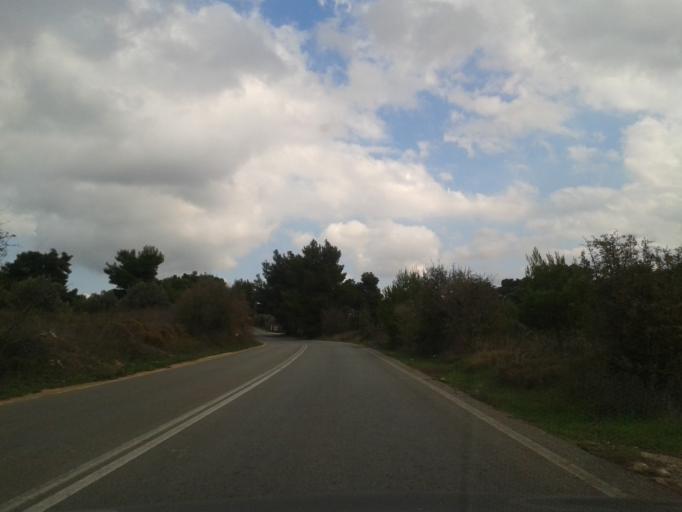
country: GR
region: Attica
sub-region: Nomarchia Anatolikis Attikis
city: Kapandriti
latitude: 38.2088
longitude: 23.8916
